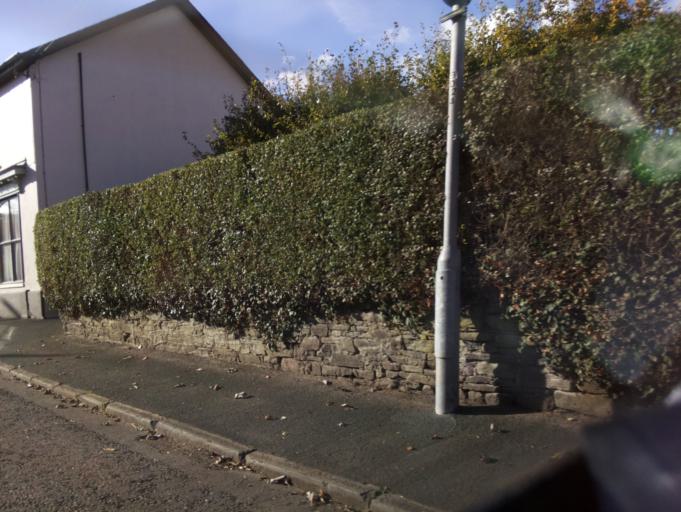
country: GB
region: Wales
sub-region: Sir Powys
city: Hay
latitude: 52.0067
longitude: -3.2491
